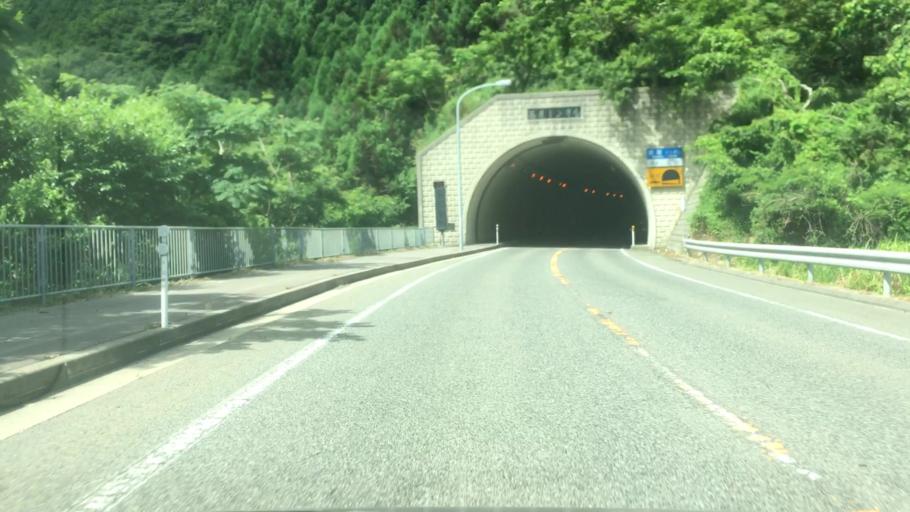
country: JP
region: Tottori
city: Tottori
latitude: 35.6173
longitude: 134.4153
